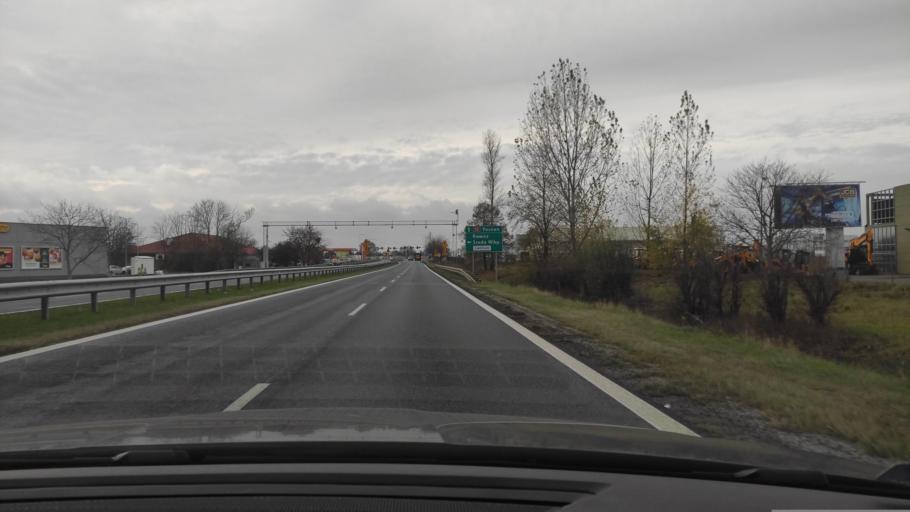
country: PL
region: Greater Poland Voivodeship
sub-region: Powiat poznanski
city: Kostrzyn
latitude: 52.3995
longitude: 17.2108
